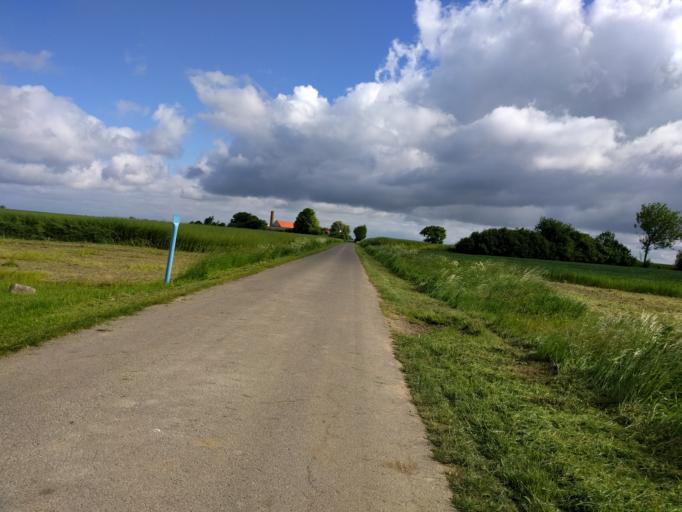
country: DK
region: South Denmark
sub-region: Kerteminde Kommune
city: Kerteminde
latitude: 55.4259
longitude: 10.6288
